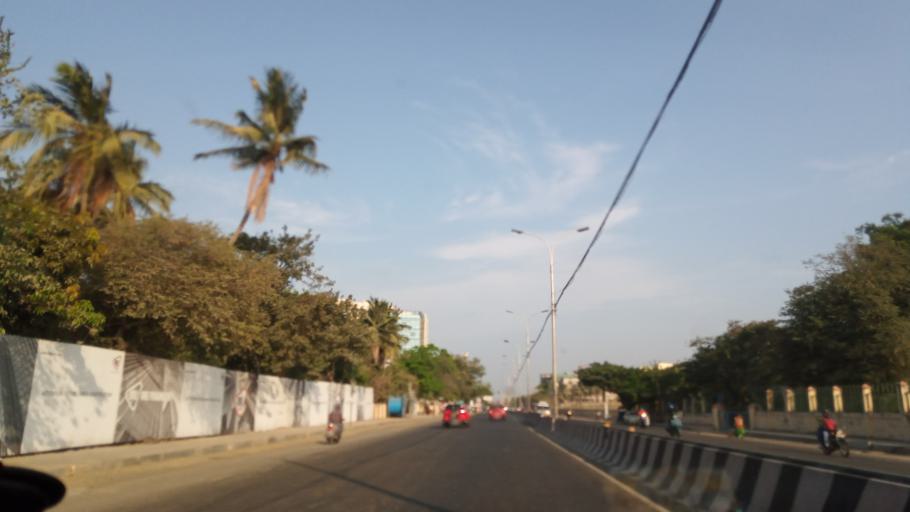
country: IN
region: Tamil Nadu
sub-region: Thiruvallur
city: Porur
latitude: 13.0306
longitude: 80.1667
